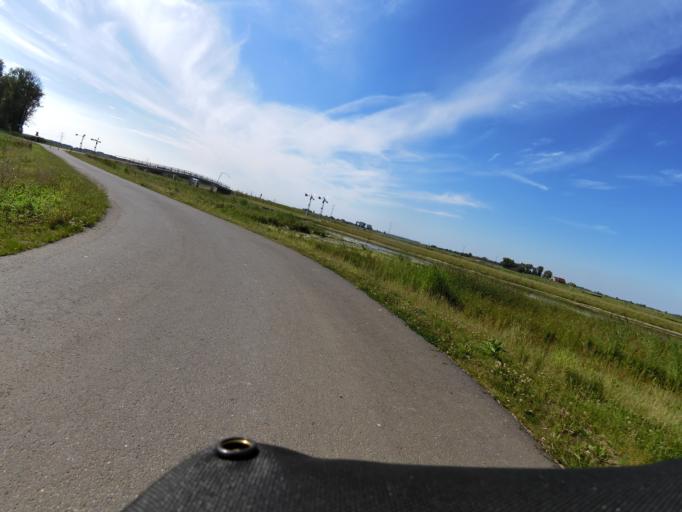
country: NL
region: South Holland
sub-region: Gemeente Hardinxveld-Giessendam
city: Neder-Hardinxveld
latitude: 51.7841
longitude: 4.8463
